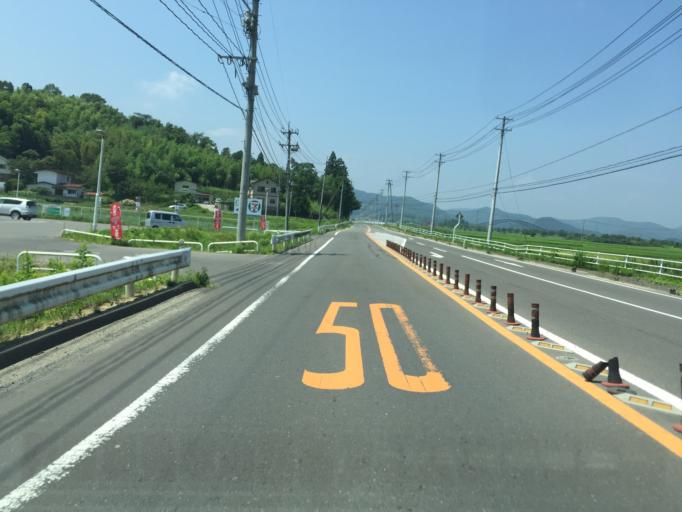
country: JP
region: Miyagi
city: Marumori
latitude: 37.9091
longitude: 140.7879
